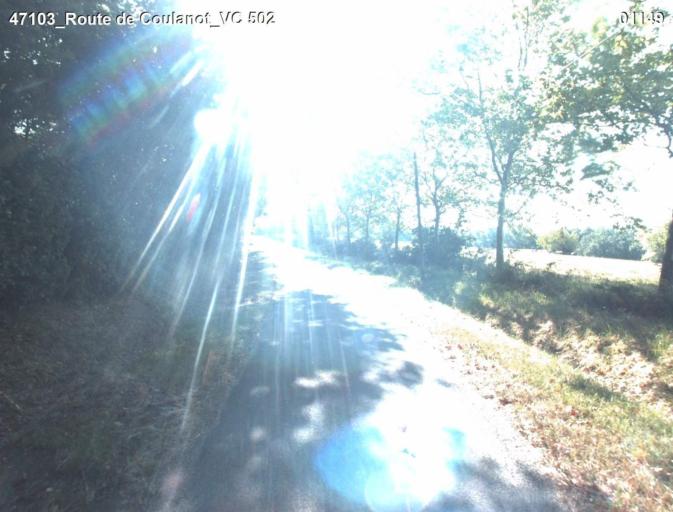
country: FR
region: Aquitaine
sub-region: Departement du Lot-et-Garonne
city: Nerac
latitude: 44.0712
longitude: 0.3415
